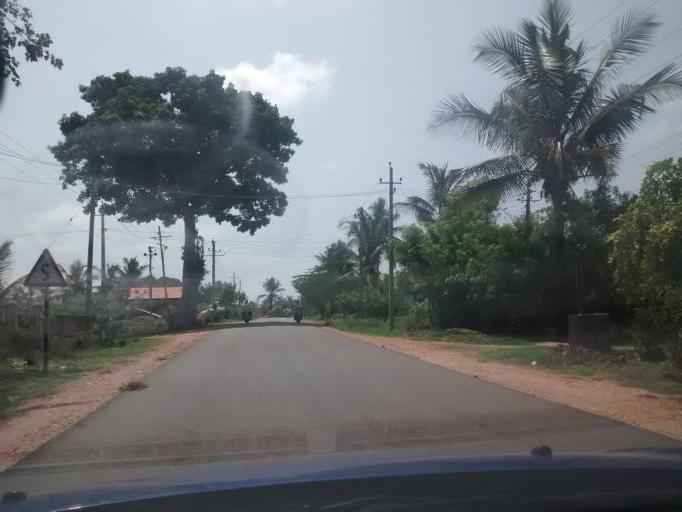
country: IN
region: Karnataka
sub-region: Hassan
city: Konanur
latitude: 12.5810
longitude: 76.2038
